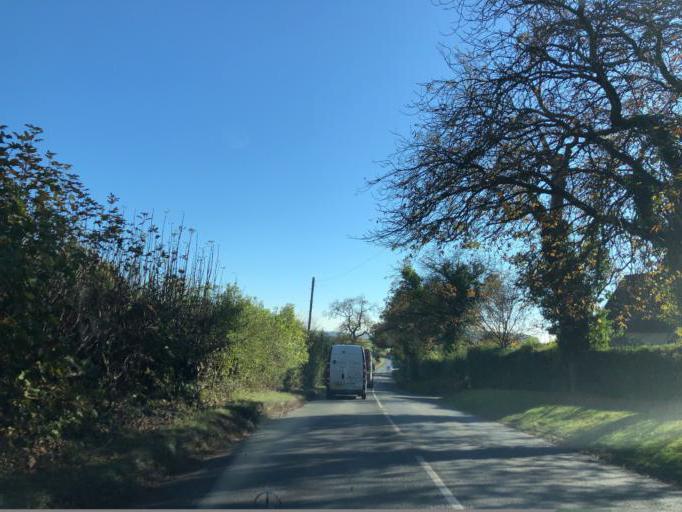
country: GB
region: England
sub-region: Warwickshire
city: Royal Leamington Spa
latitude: 52.2583
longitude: -1.5299
